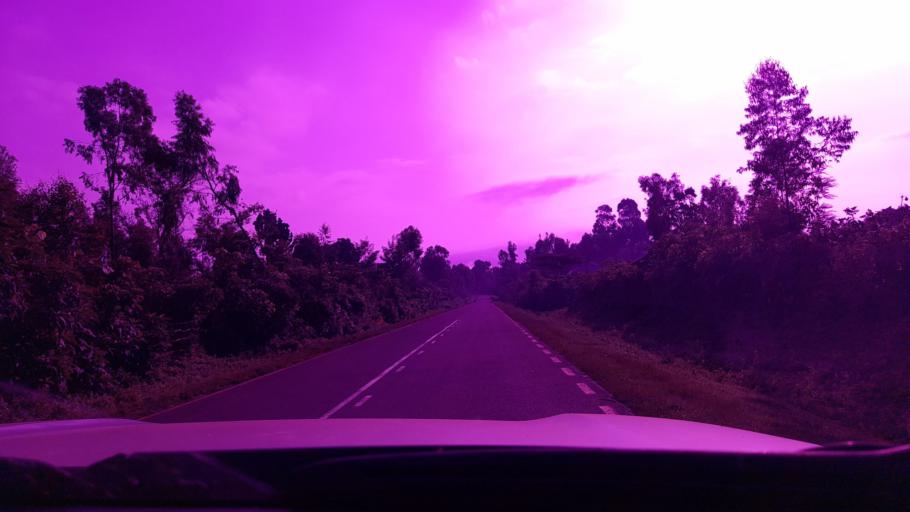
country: ET
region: Oromiya
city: Bedele
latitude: 8.1540
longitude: 36.4707
